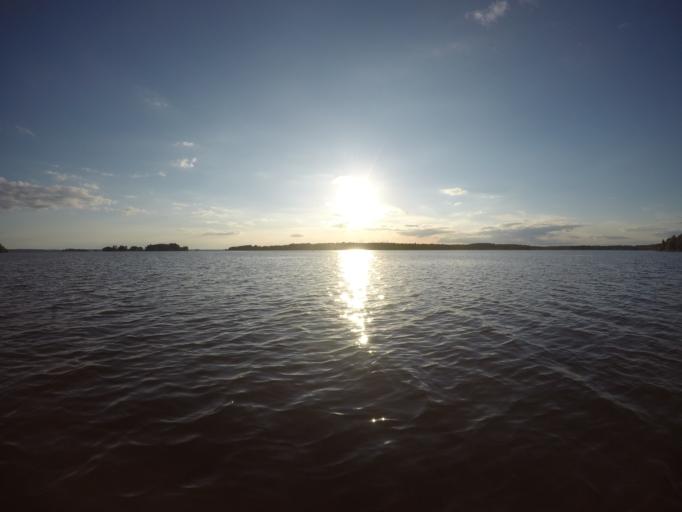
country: SE
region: Vaestmanland
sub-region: Hallstahammars Kommun
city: Kolback
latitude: 59.4610
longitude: 16.2079
